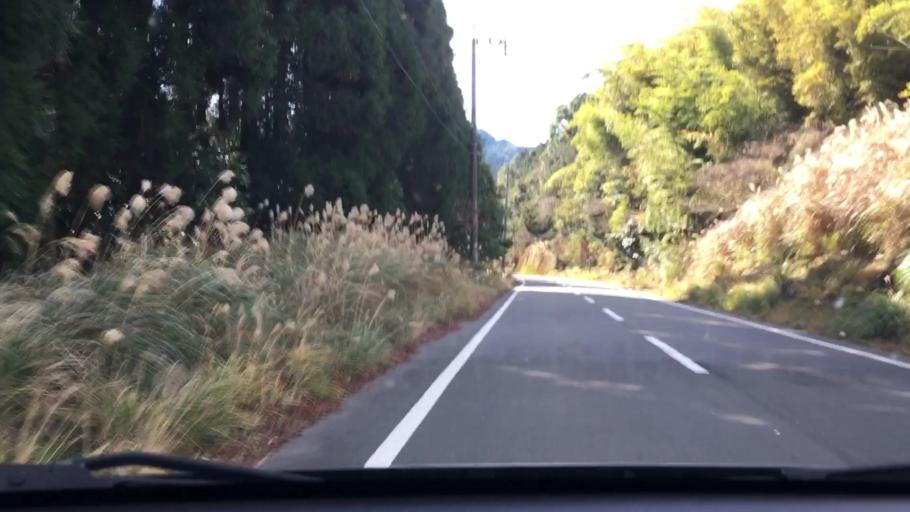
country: JP
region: Kagoshima
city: Ijuin
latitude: 31.7152
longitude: 130.4260
